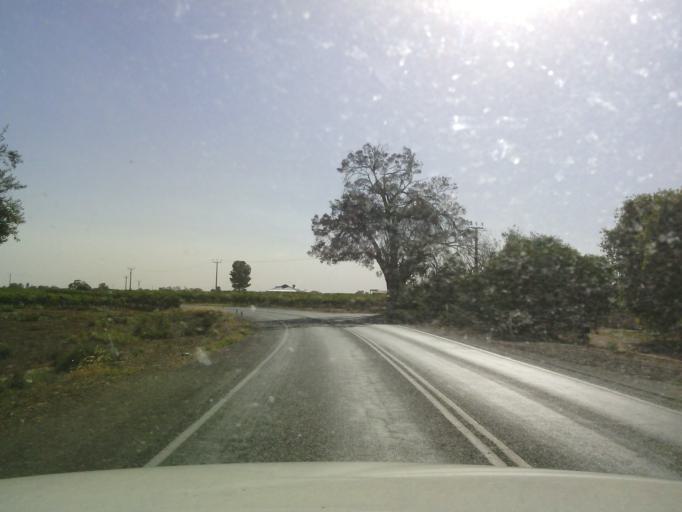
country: AU
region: South Australia
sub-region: Berri and Barmera
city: Berri
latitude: -34.2809
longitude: 140.5667
